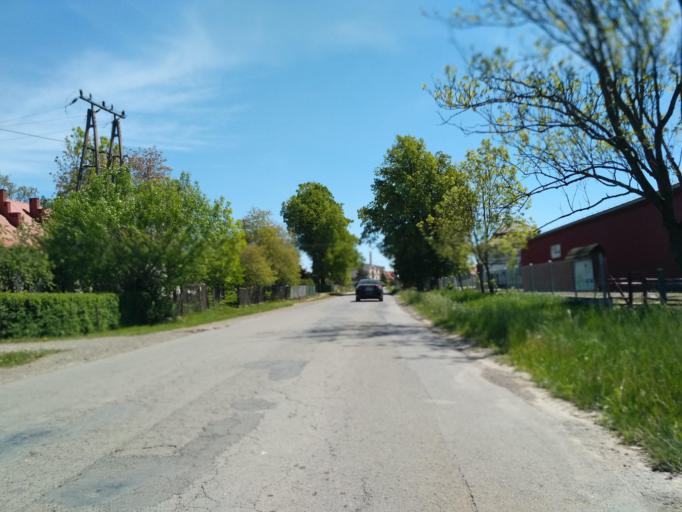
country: PL
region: Subcarpathian Voivodeship
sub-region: Powiat krosnienski
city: Sieniawa
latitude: 49.5411
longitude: 21.9647
